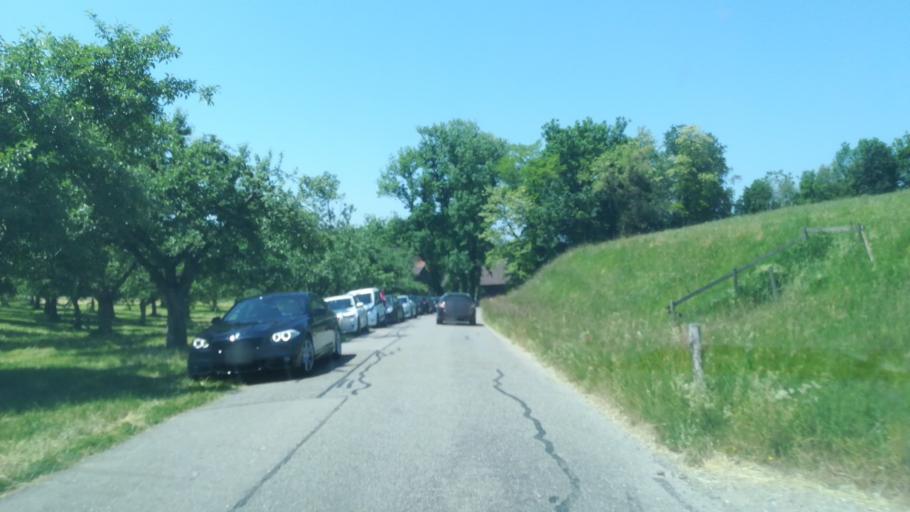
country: CH
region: Thurgau
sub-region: Frauenfeld District
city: Pfyn
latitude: 47.6288
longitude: 8.9272
